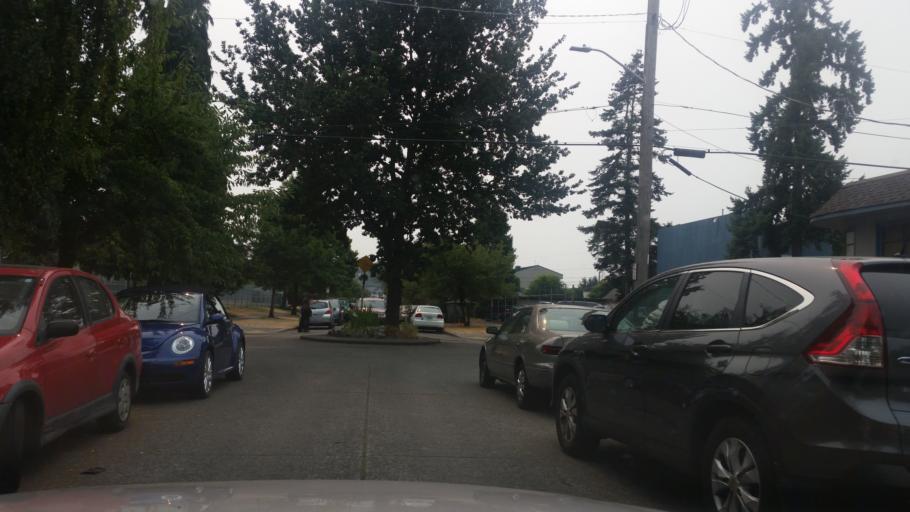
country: US
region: Washington
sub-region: King County
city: Seattle
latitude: 47.6681
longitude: -122.3708
